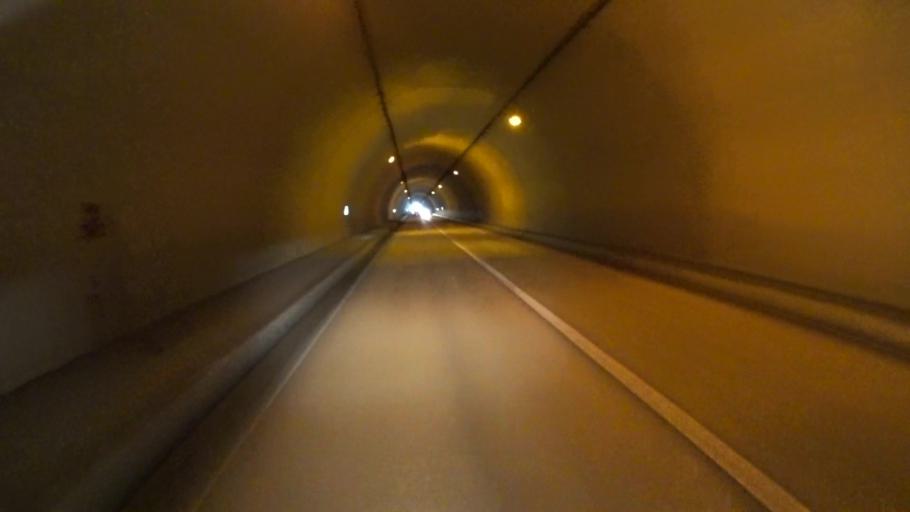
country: JP
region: Hyogo
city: Toyooka
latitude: 35.5278
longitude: 134.9835
